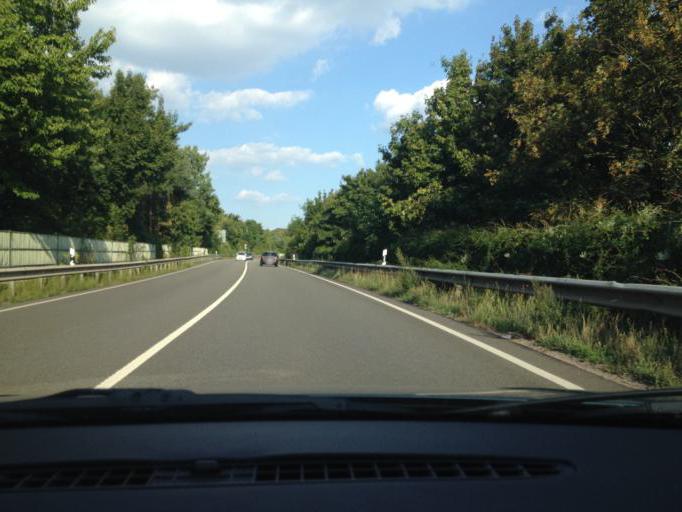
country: DE
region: Rheinland-Pfalz
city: Dudenhofen
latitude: 49.3181
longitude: 8.3903
